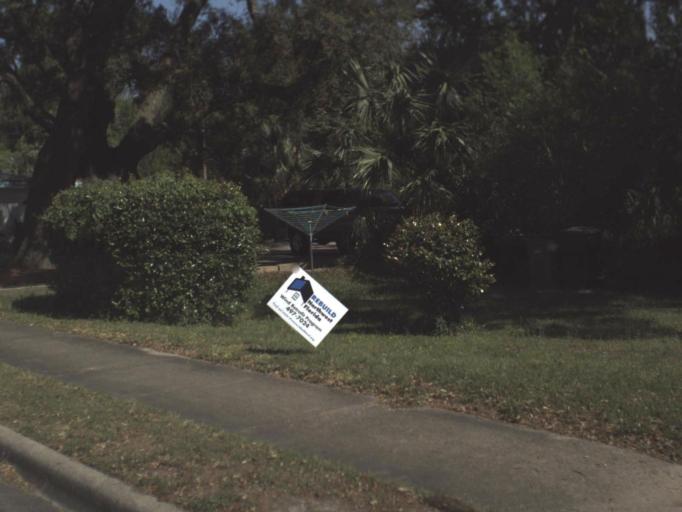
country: US
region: Florida
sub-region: Escambia County
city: Pensacola
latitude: 30.4205
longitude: -87.2221
